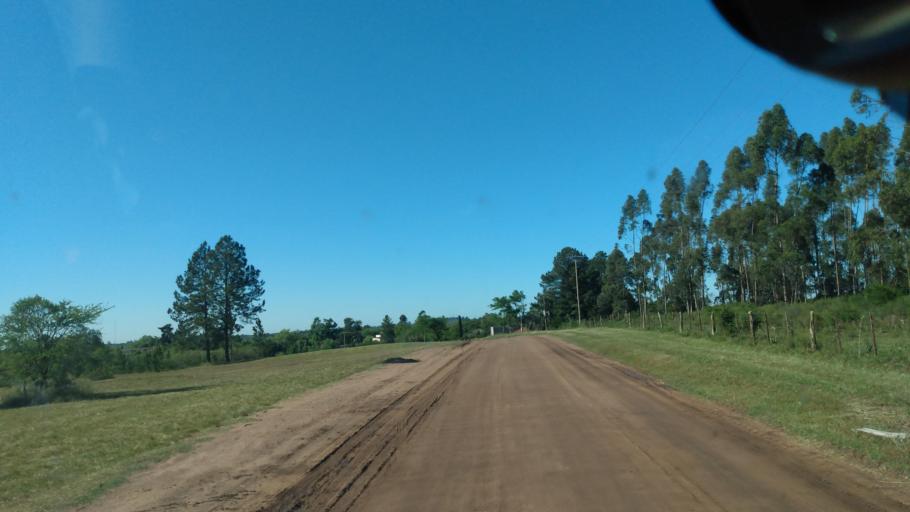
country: AR
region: Entre Rios
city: Colon
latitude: -32.1516
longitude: -58.1964
